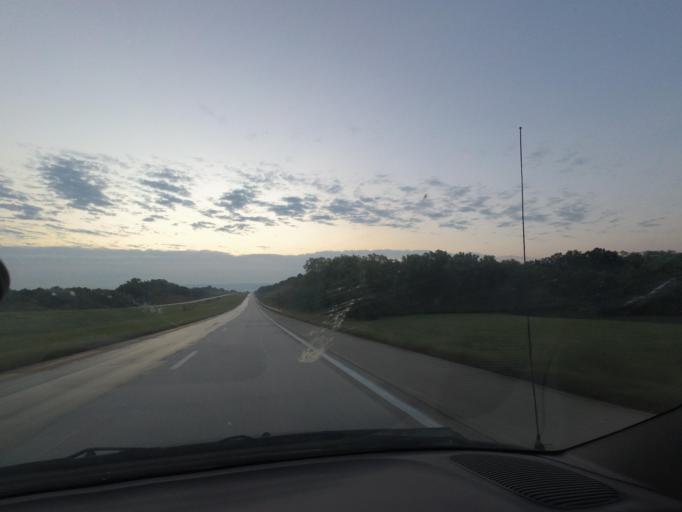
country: US
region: Missouri
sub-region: Macon County
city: Macon
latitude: 39.7590
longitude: -92.6611
